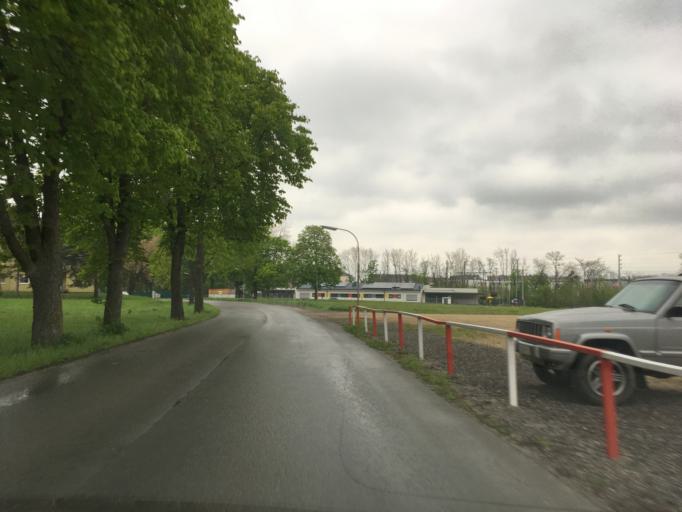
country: AT
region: Burgenland
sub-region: Politischer Bezirk Neusiedl am See
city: Bruckneudorf
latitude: 48.0166
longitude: 16.7843
